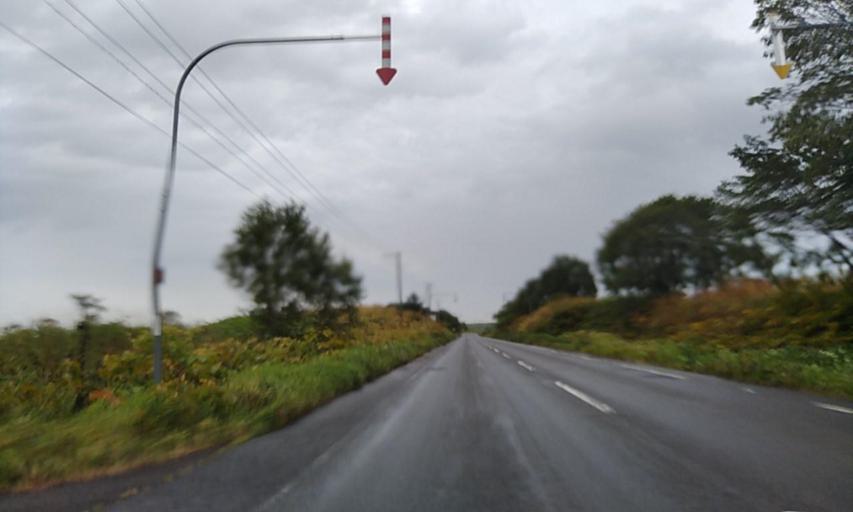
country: JP
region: Hokkaido
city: Mombetsu
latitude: 44.5091
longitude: 143.0734
